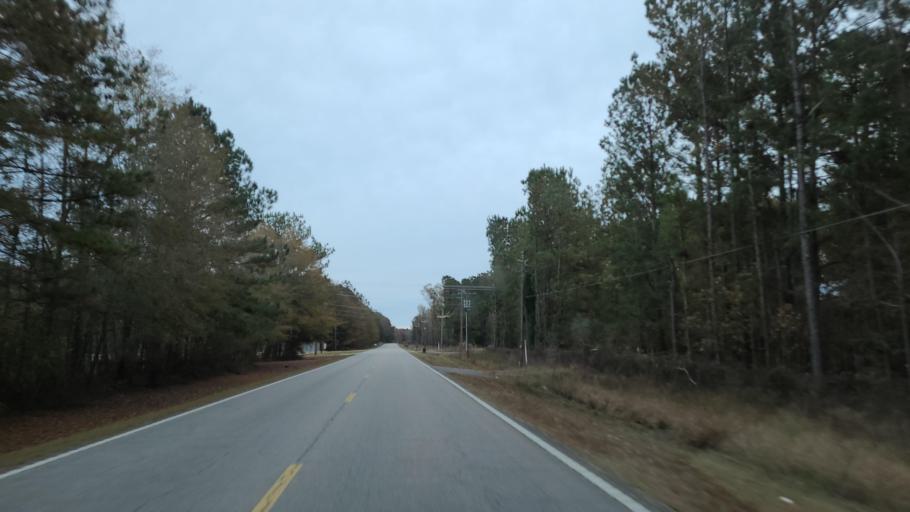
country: US
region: Mississippi
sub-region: Clarke County
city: Stonewall
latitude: 32.0269
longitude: -88.8603
